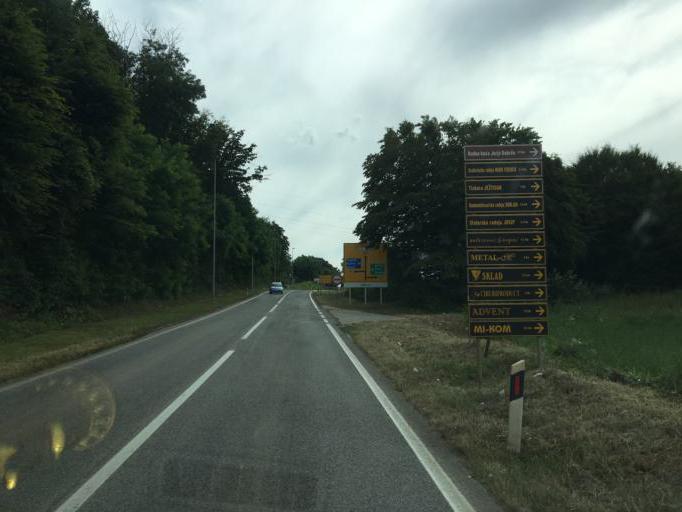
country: HR
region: Istarska
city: Pazin
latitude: 45.2308
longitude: 13.9171
